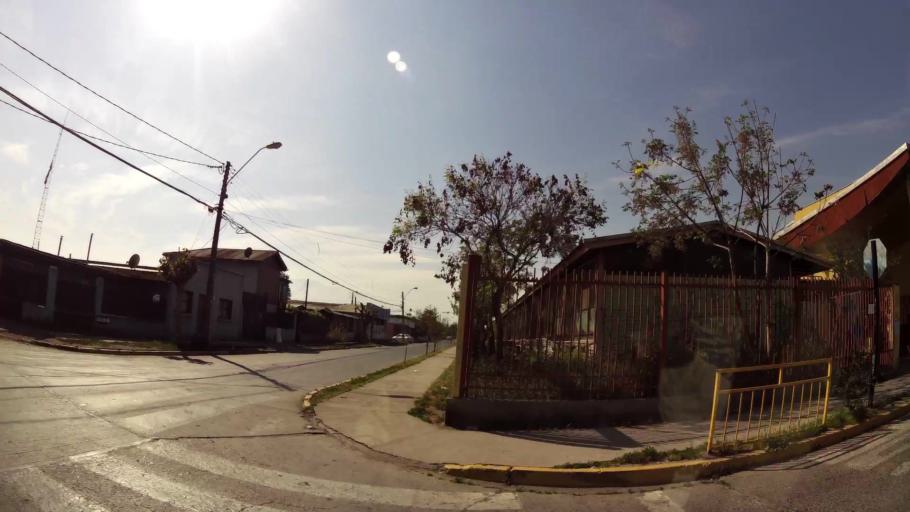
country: CL
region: Santiago Metropolitan
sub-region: Provincia de Santiago
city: La Pintana
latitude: -33.5622
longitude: -70.6647
